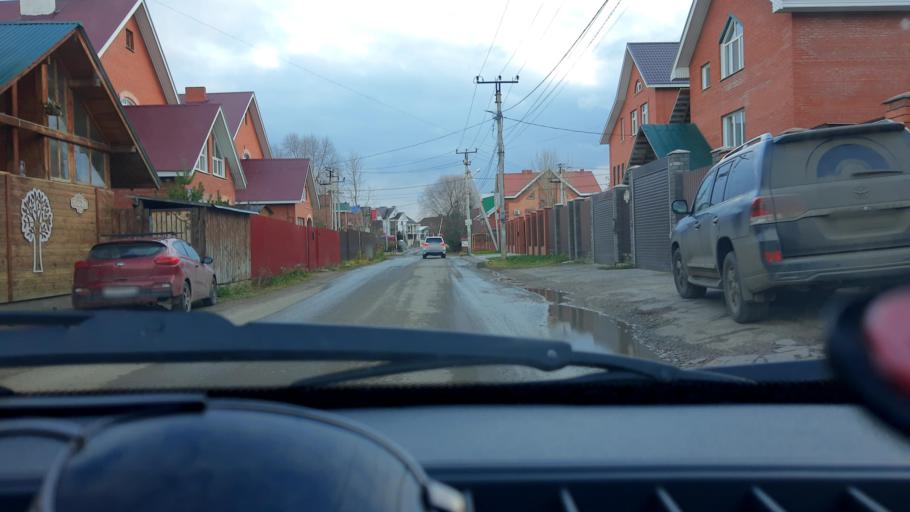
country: RU
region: Bashkortostan
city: Ufa
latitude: 54.6919
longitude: 55.9778
